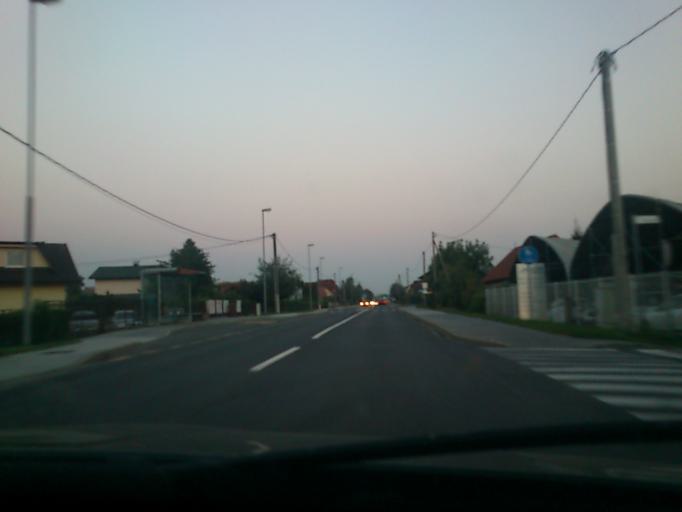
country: SI
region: Miklavz na Dravskem Polju
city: Miklavz na Dravskem Polju
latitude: 46.5058
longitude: 15.6983
